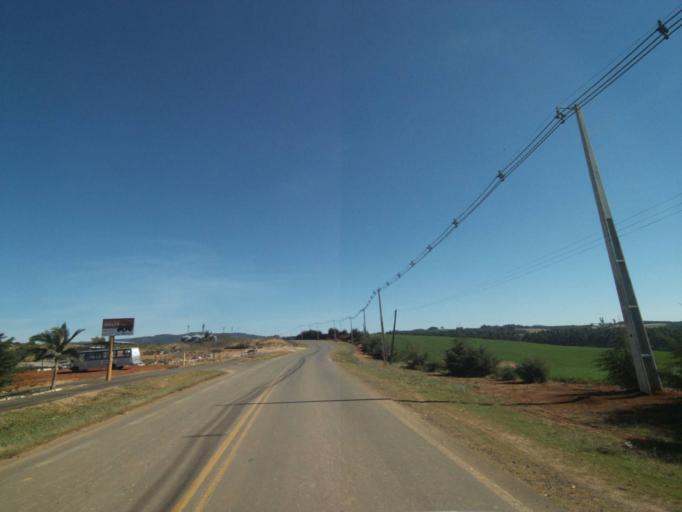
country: BR
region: Parana
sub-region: Tibagi
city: Tibagi
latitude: -24.5232
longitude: -50.4319
